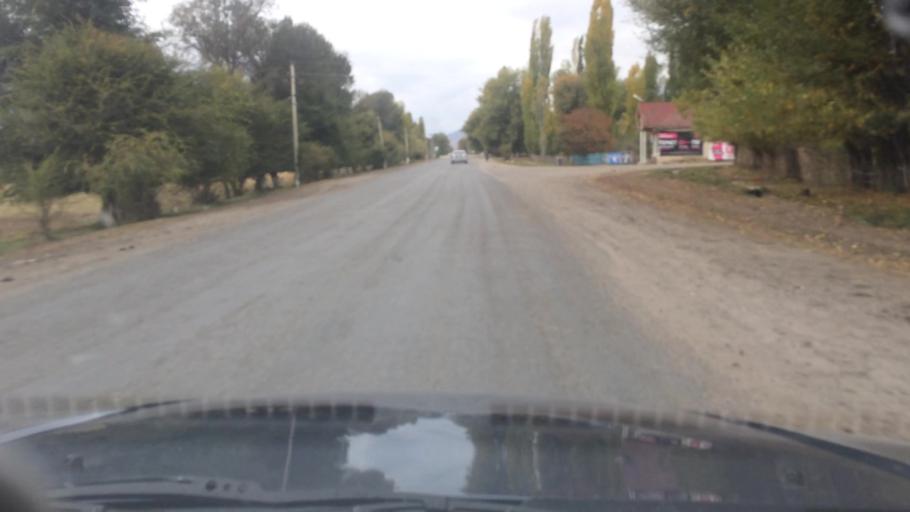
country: KG
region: Ysyk-Koel
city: Tyup
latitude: 42.7867
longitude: 78.2584
